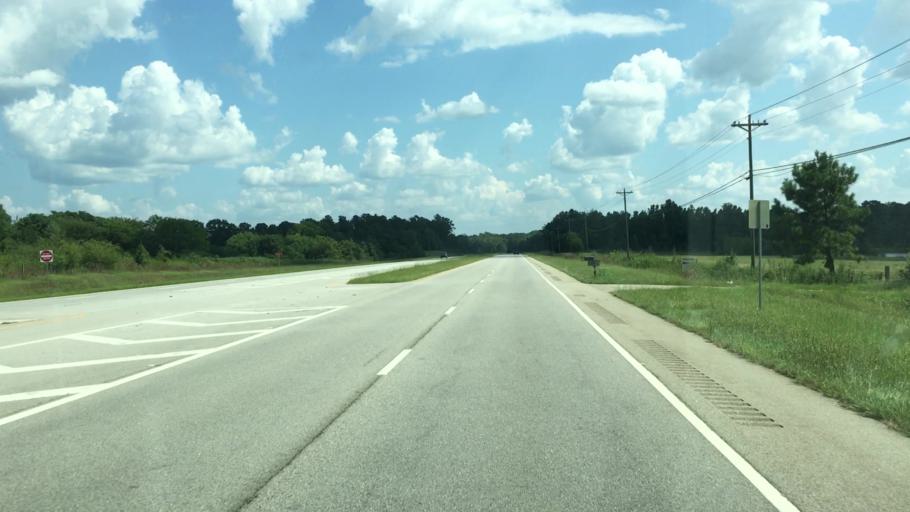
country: US
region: Georgia
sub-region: Putnam County
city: Eatonton
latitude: 33.2495
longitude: -83.3267
